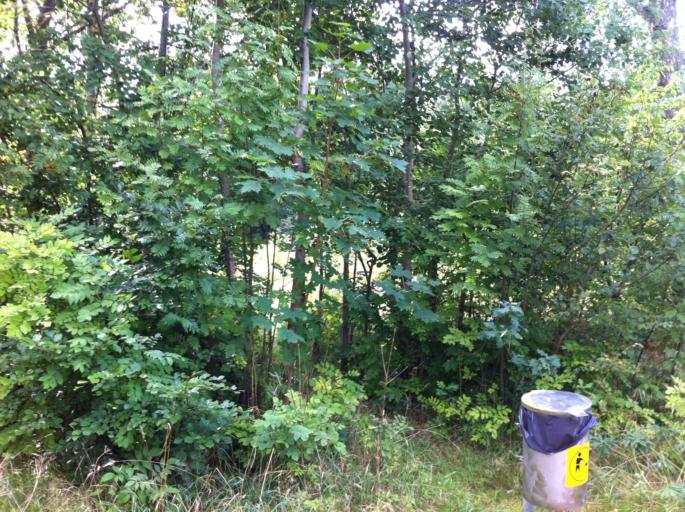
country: SE
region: Halland
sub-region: Hylte Kommun
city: Hyltebruk
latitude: 56.9973
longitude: 13.2459
